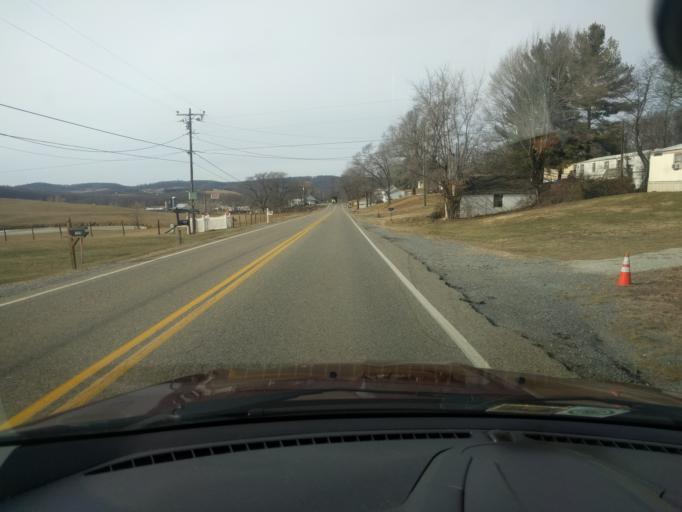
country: US
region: Virginia
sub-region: Augusta County
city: Stuarts Draft
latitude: 38.0399
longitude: -79.0797
